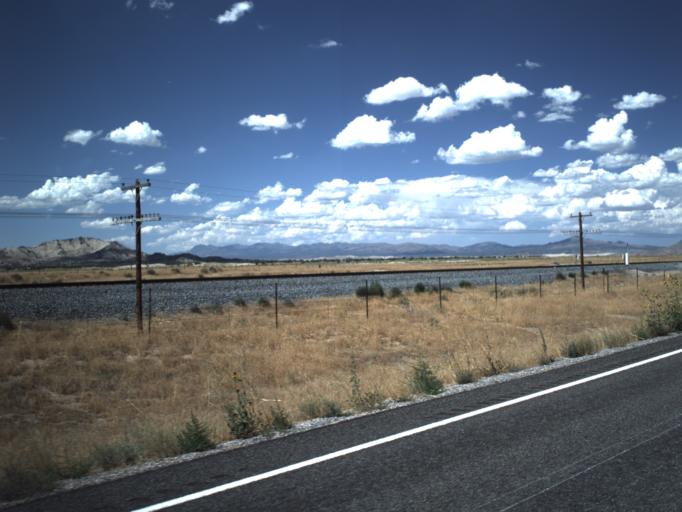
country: US
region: Utah
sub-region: Millard County
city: Delta
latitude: 39.5602
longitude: -112.3502
